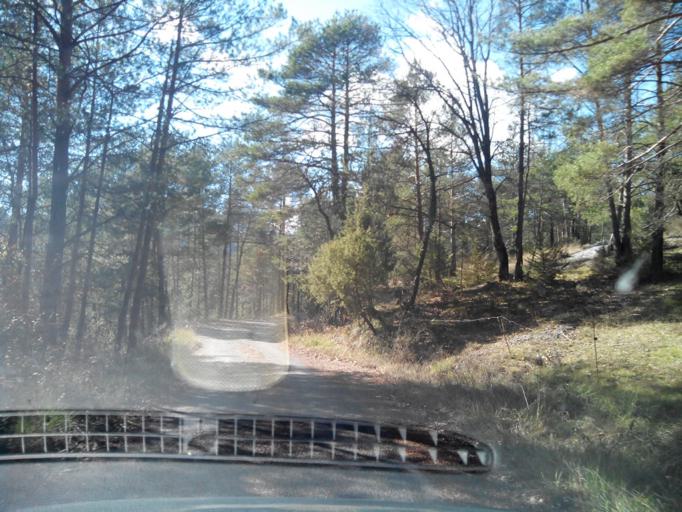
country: ES
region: Catalonia
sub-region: Provincia de Barcelona
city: Vilada
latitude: 42.1306
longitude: 1.9293
